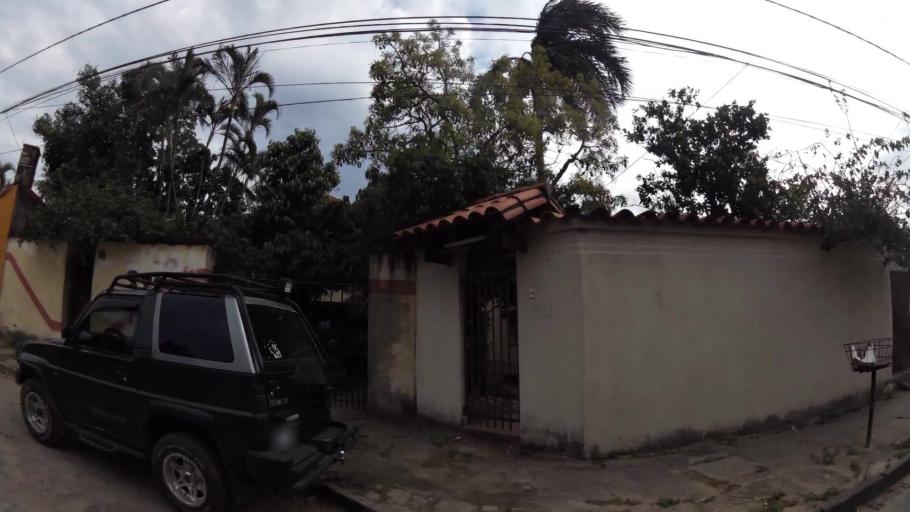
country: BO
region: Santa Cruz
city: Santa Cruz de la Sierra
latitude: -17.7970
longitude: -63.2011
